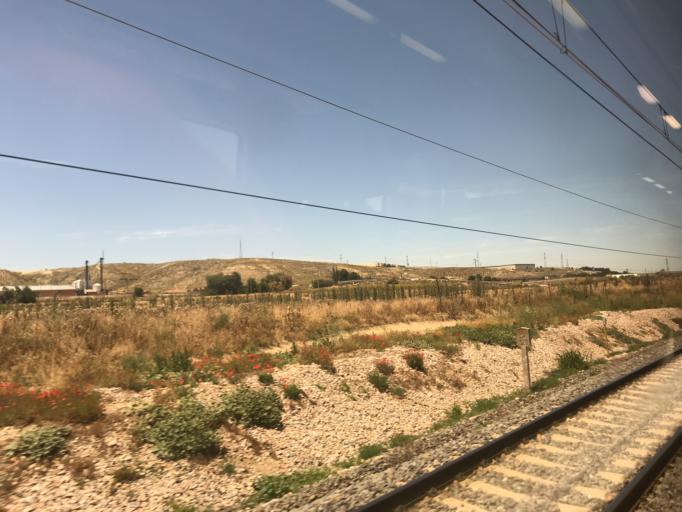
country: ES
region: Madrid
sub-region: Provincia de Madrid
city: Aranjuez
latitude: 40.0847
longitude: -3.6330
